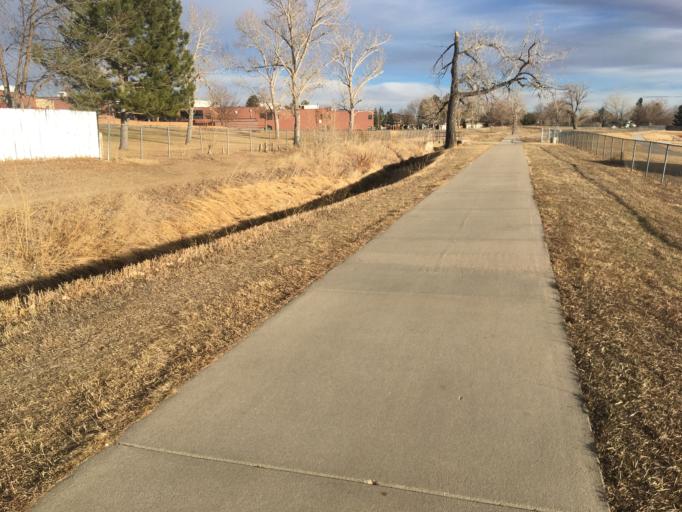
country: US
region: Colorado
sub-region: Broomfield County
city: Broomfield
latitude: 39.9375
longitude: -105.0802
